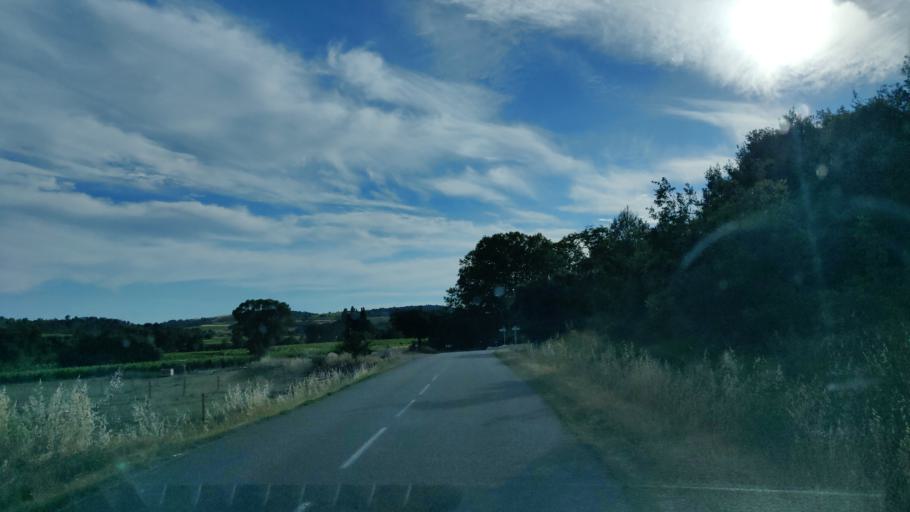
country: FR
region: Languedoc-Roussillon
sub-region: Departement de l'Herault
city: Combaillaux
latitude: 43.6680
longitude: 3.7828
